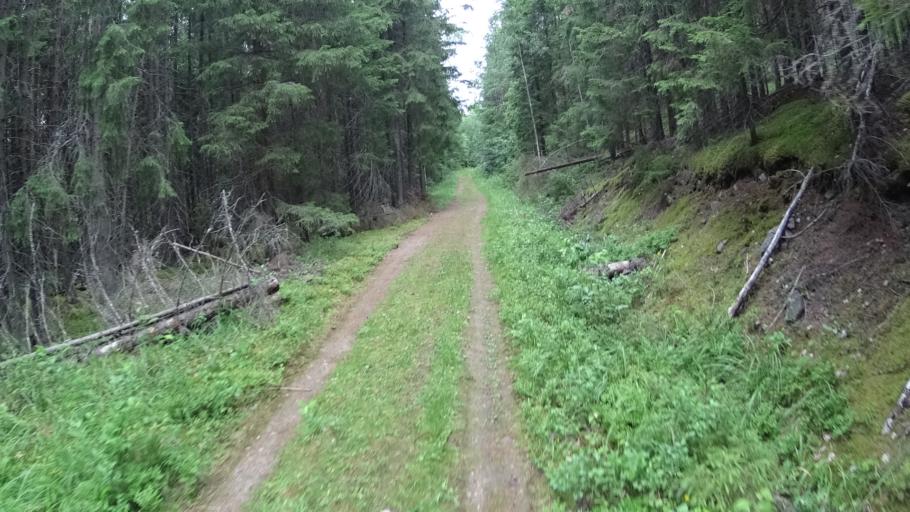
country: FI
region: Southern Savonia
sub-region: Mikkeli
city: Maentyharju
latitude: 61.1865
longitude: 26.8279
